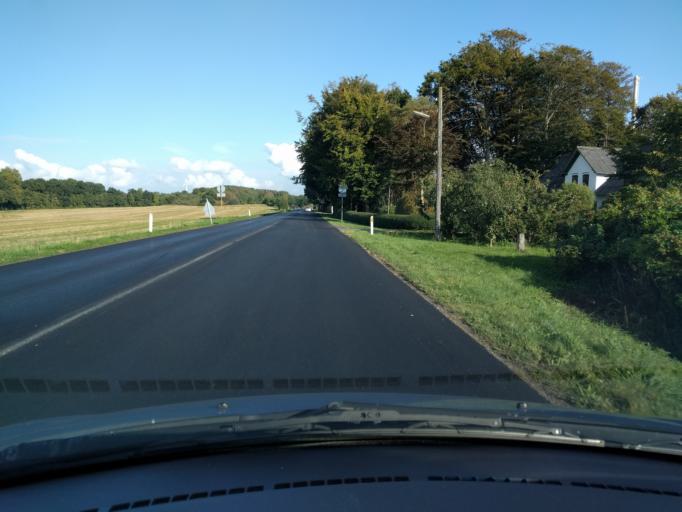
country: DK
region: South Denmark
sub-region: Assens Kommune
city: Glamsbjerg
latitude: 55.2693
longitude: 10.1261
